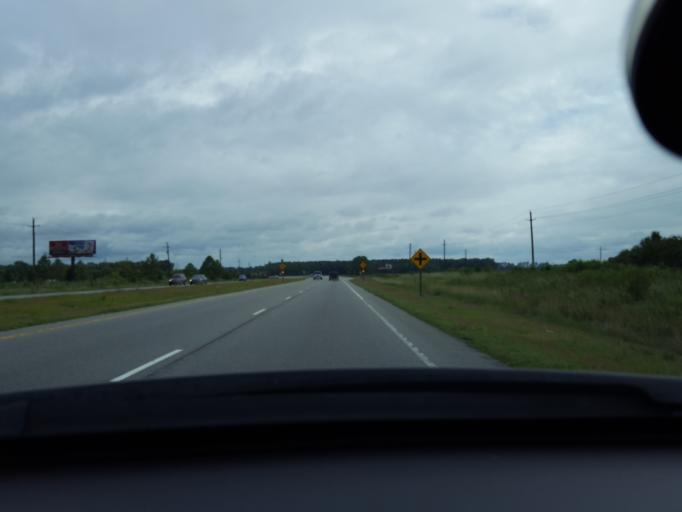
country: US
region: North Carolina
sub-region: Pitt County
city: Ayden
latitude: 35.4691
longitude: -77.4359
